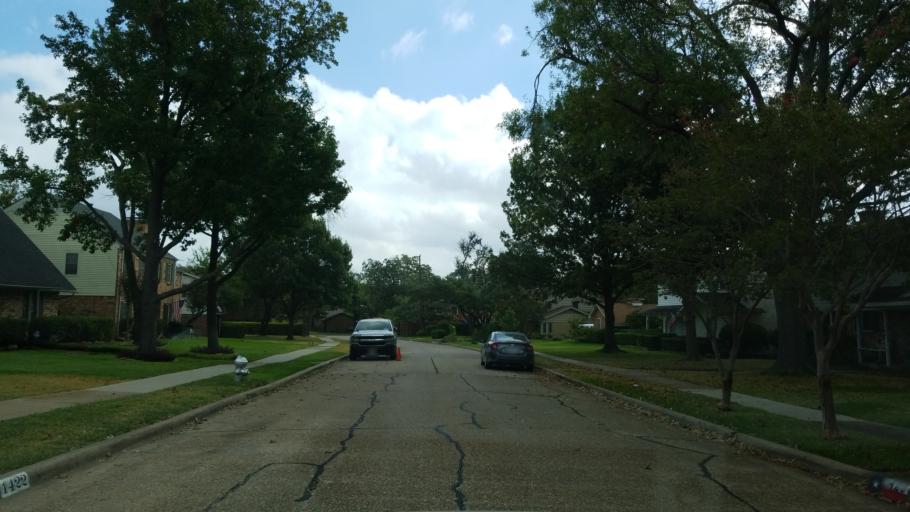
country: US
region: Texas
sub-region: Dallas County
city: Richardson
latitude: 32.9474
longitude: -96.7674
